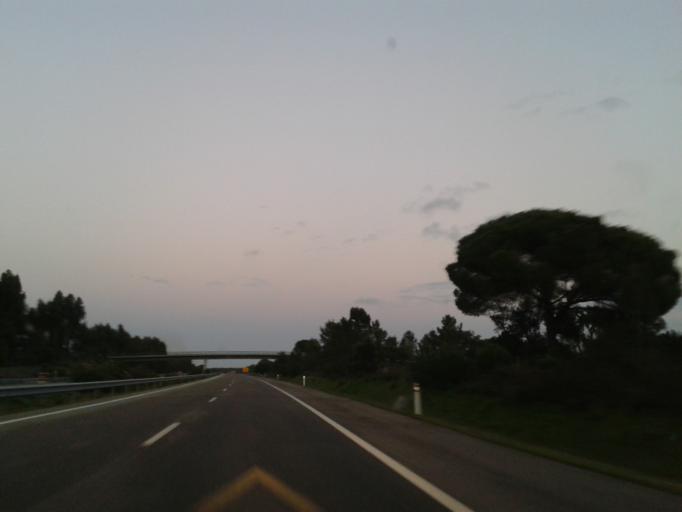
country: PT
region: Evora
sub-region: Vendas Novas
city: Vendas Novas
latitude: 38.6348
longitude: -8.5159
